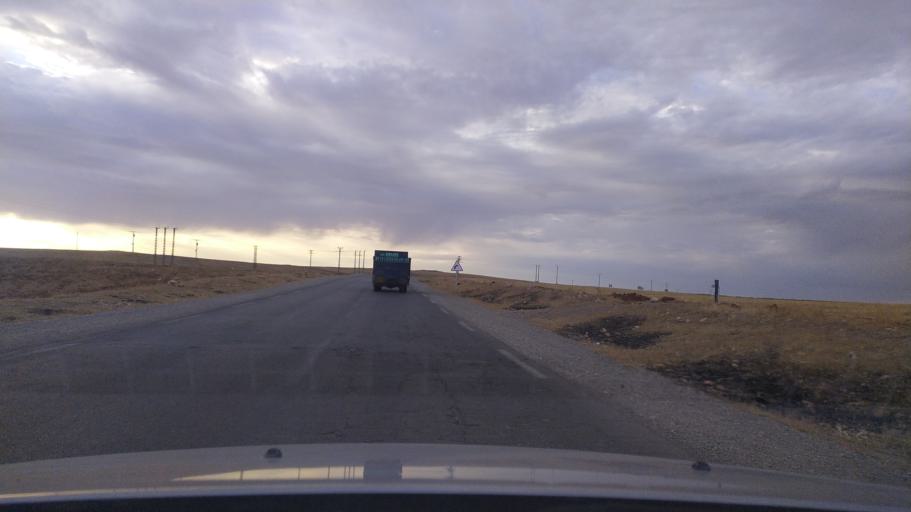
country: DZ
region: Tiaret
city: Frenda
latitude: 34.9872
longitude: 1.1344
